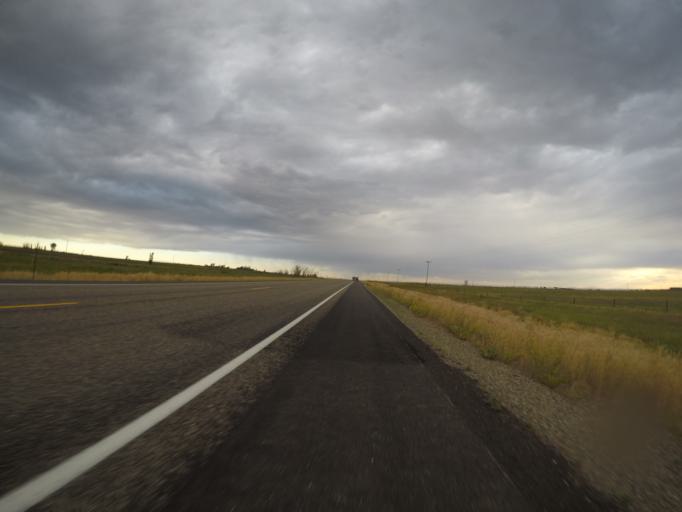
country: US
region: Wyoming
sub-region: Albany County
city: Laramie
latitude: 41.7904
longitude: -105.9836
